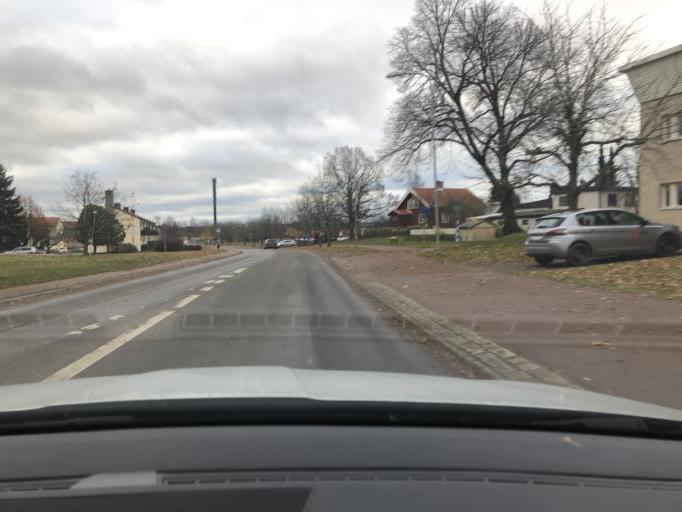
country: SE
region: Uppsala
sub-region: Tierps Kommun
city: Tierp
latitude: 60.3419
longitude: 17.5121
